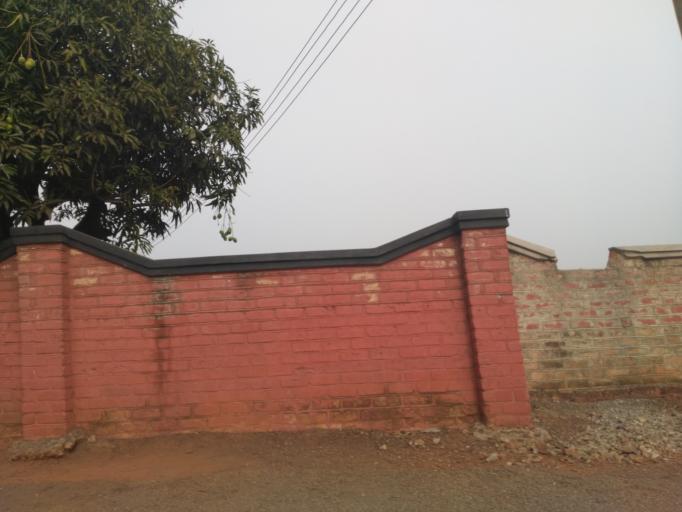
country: GH
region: Ashanti
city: Kumasi
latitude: 6.6934
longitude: -1.6247
